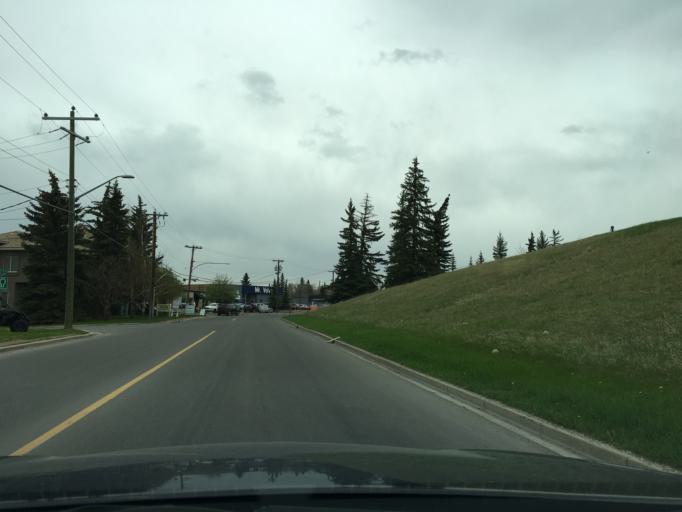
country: CA
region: Alberta
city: Calgary
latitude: 50.9873
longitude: -114.0656
